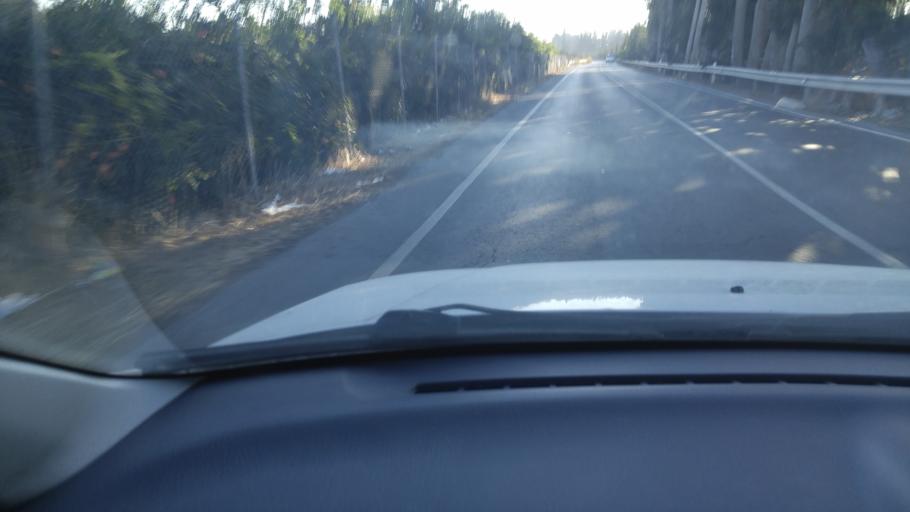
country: CY
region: Limassol
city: Ypsonas
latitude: 34.6535
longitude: 32.9825
